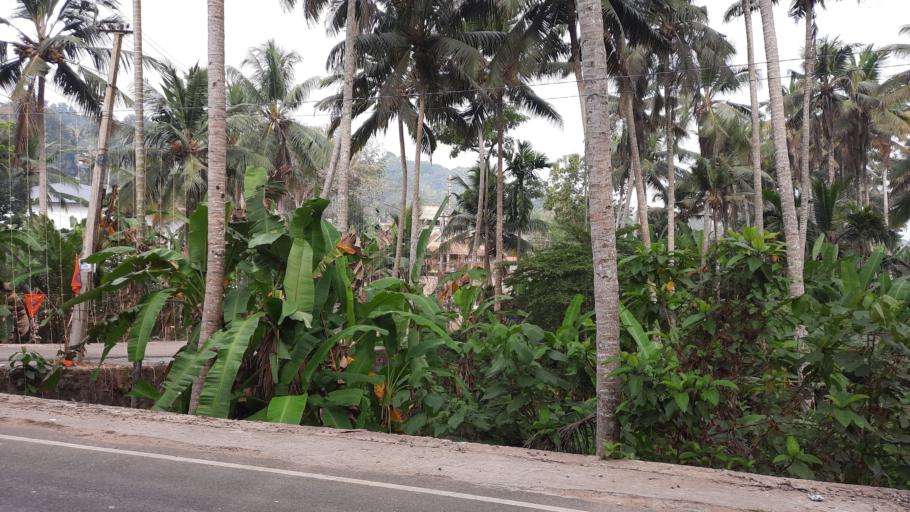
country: IN
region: Kerala
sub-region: Thiruvananthapuram
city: Nedumangad
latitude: 8.5819
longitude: 76.9287
